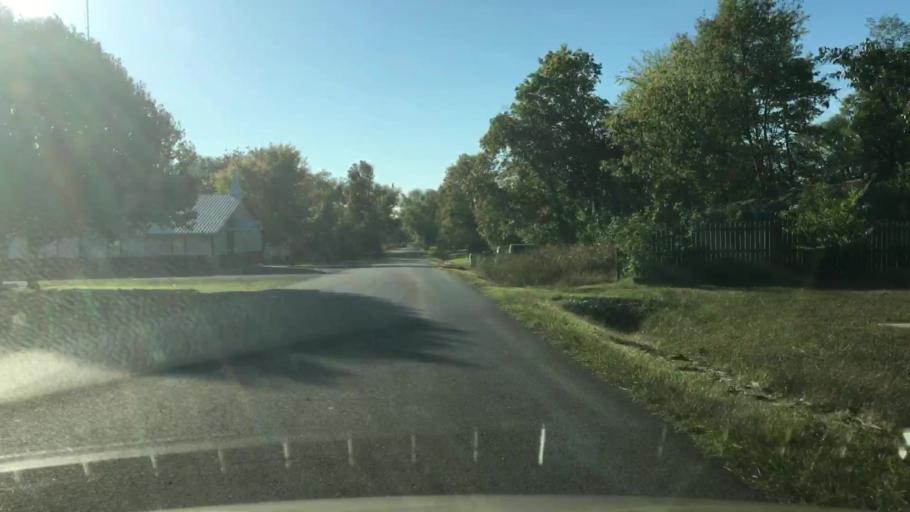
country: US
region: Oklahoma
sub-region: Cherokee County
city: Tahlequah
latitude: 35.9297
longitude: -95.1390
